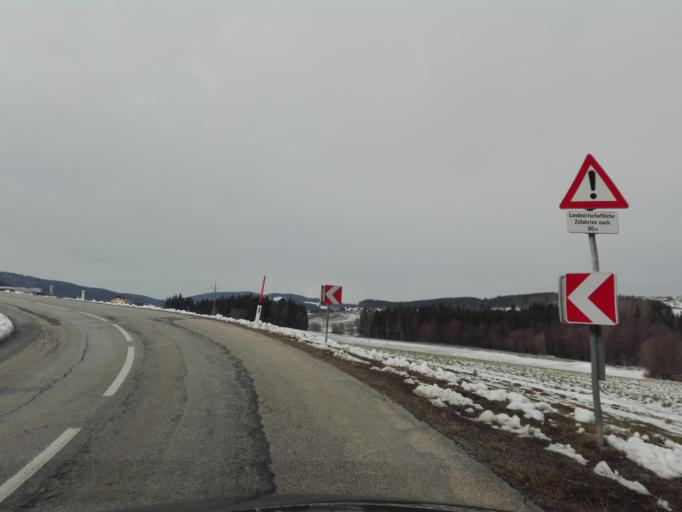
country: AT
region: Upper Austria
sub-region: Politischer Bezirk Rohrbach
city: Atzesberg
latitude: 48.4991
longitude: 13.8908
